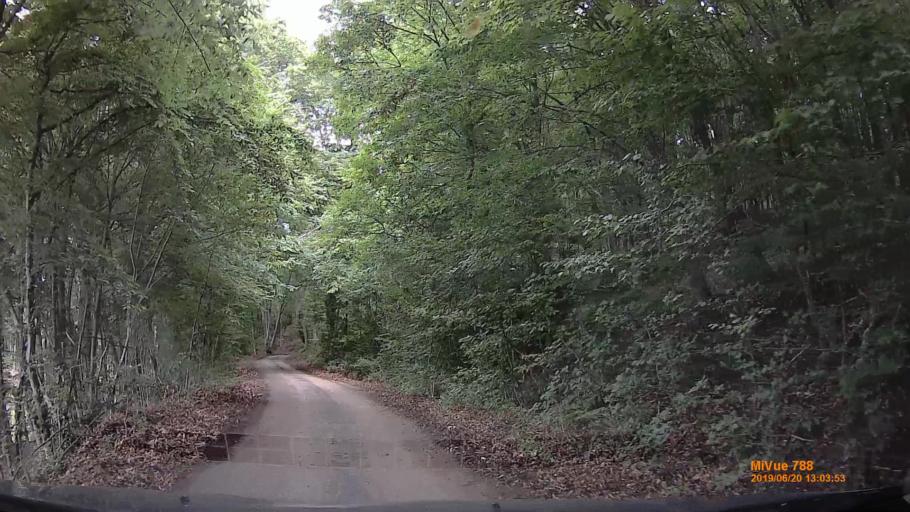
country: HU
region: Baranya
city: Hosszuheteny
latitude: 46.2127
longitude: 18.3621
